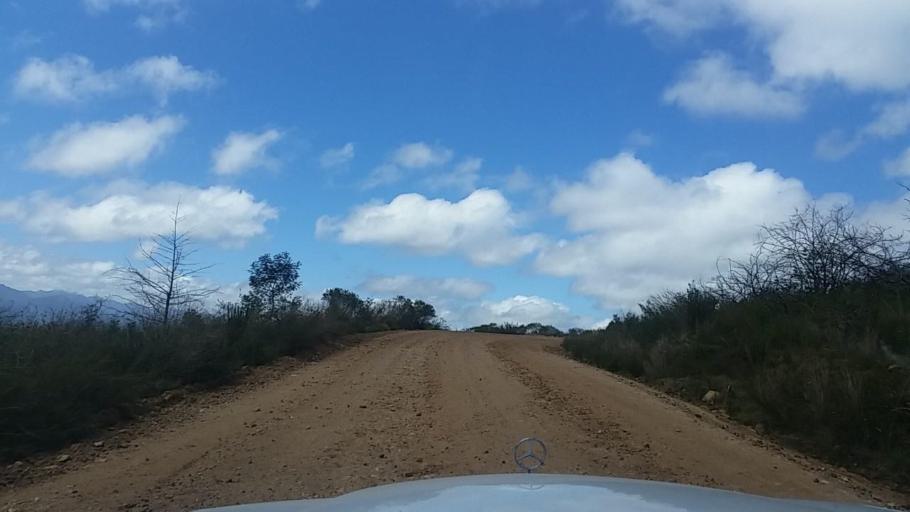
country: ZA
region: Western Cape
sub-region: Eden District Municipality
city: Knysna
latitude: -33.8849
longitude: 23.1587
